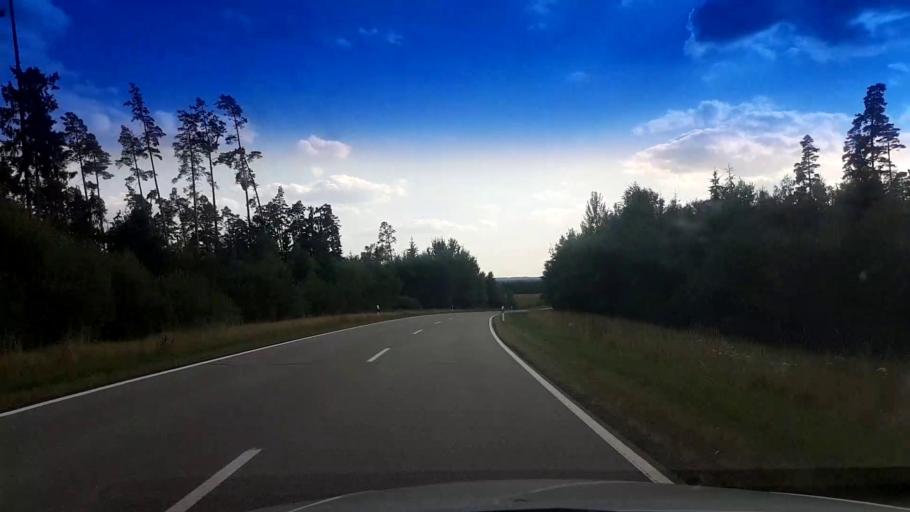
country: DE
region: Bavaria
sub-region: Upper Palatinate
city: Tirschenreuth
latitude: 49.8931
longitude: 12.3719
